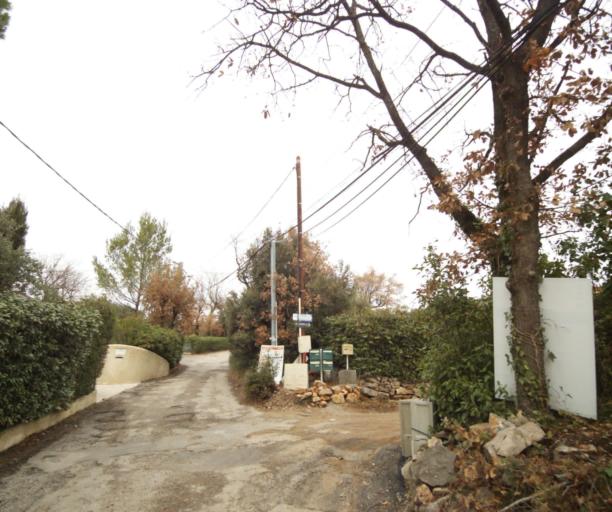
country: FR
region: Provence-Alpes-Cote d'Azur
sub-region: Departement du Var
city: Trans-en-Provence
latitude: 43.5095
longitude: 6.4910
